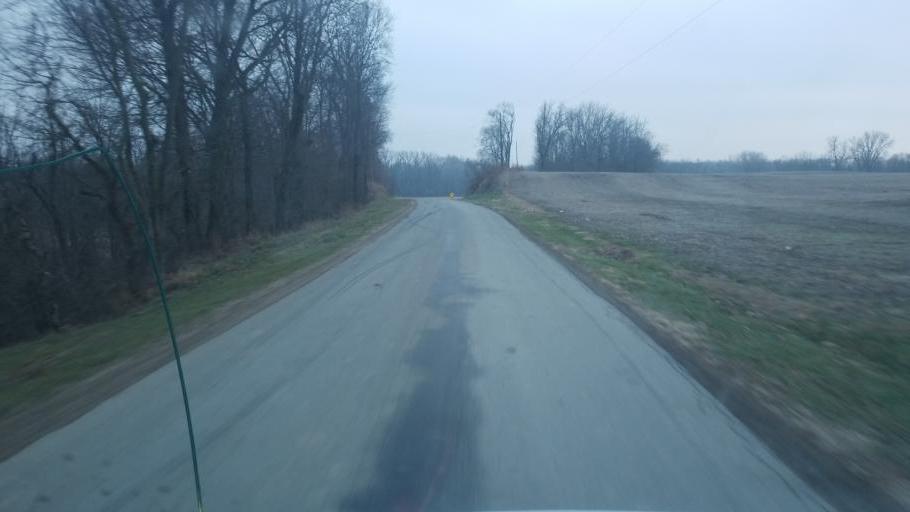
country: US
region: Ohio
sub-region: Seneca County
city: Tiffin
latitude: 40.9916
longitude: -83.2048
